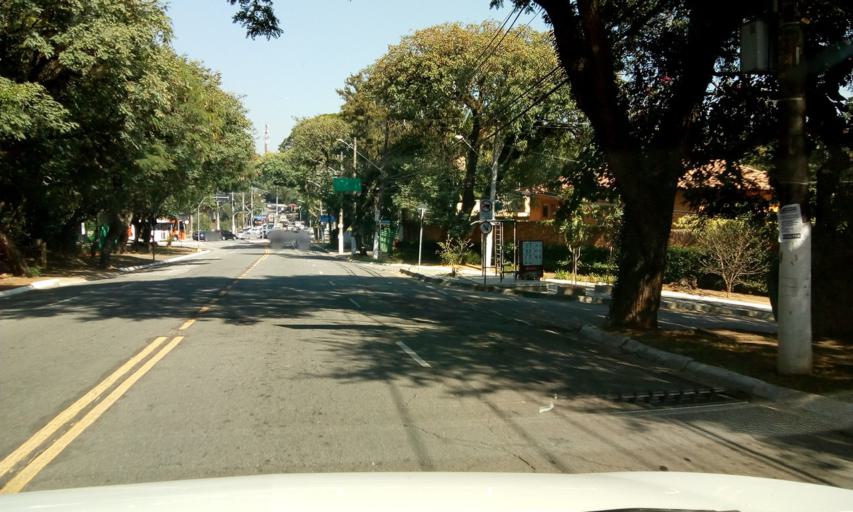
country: BR
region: Sao Paulo
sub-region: Sao Paulo
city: Sao Paulo
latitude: -23.5938
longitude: -46.7067
